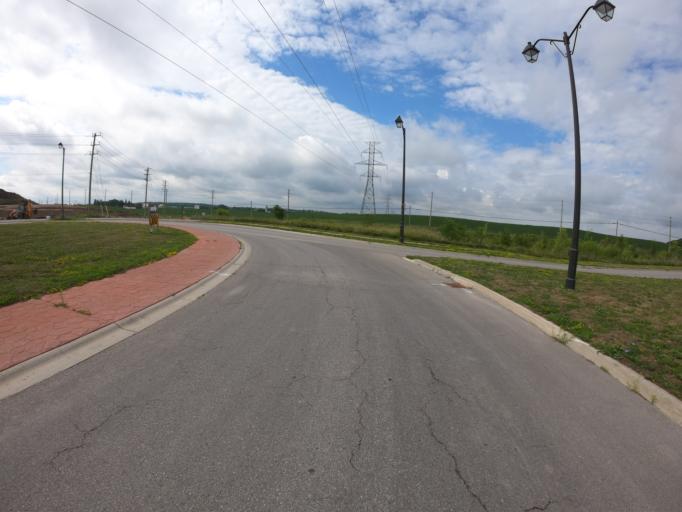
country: CA
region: Ontario
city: Waterloo
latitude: 43.4494
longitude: -80.5911
